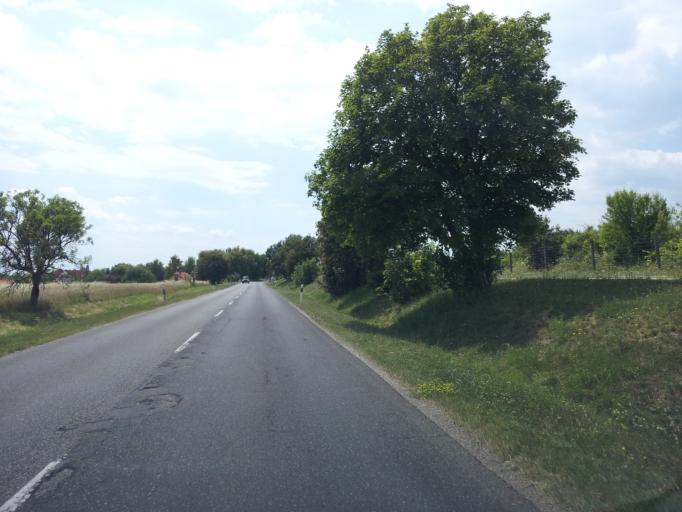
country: HU
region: Veszprem
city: Tihany
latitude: 46.9091
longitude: 17.8113
